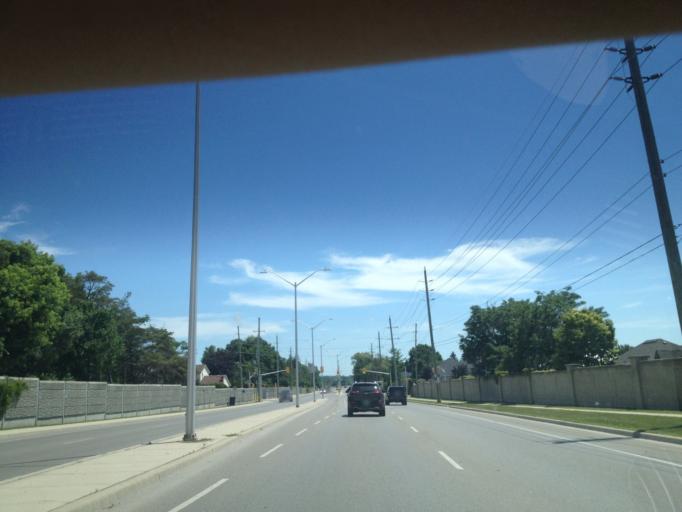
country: CA
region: Ontario
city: London
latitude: 42.9841
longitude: -81.3248
